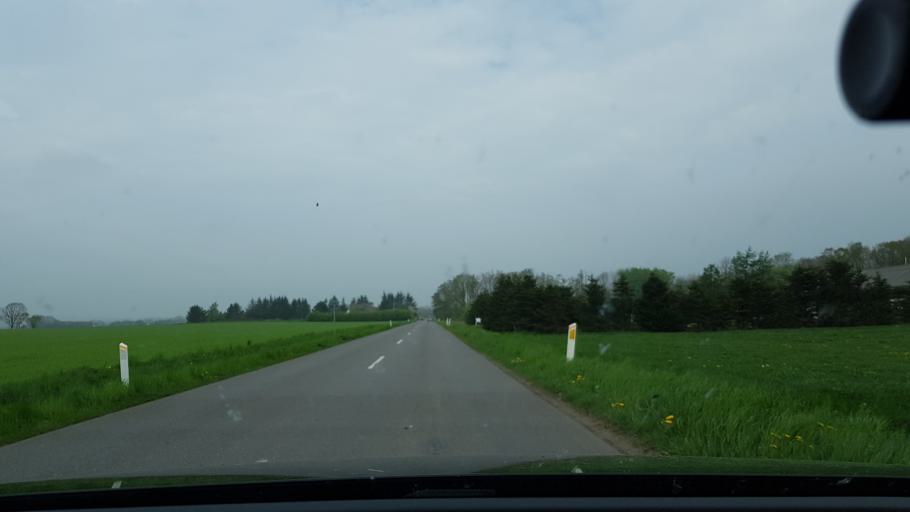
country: DK
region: Capital Region
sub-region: Bornholm Kommune
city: Nexo
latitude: 55.0161
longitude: 15.0962
